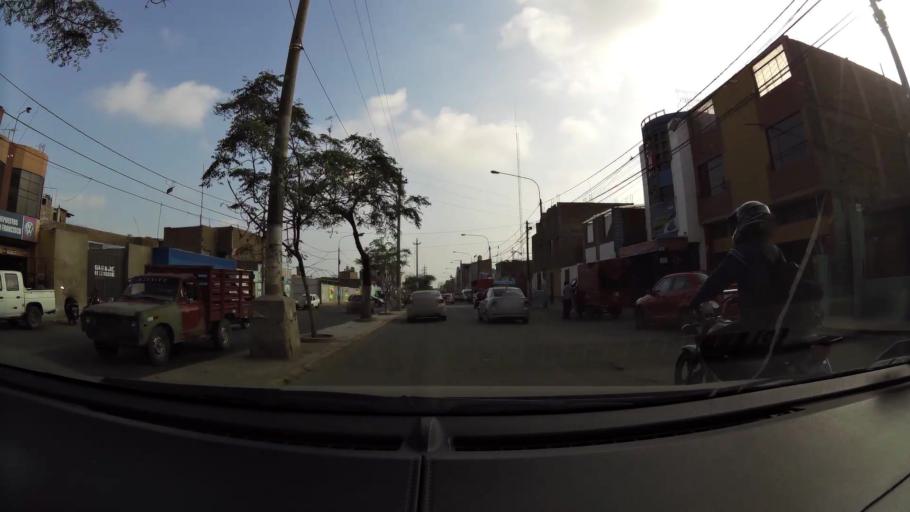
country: PE
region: La Libertad
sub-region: Provincia de Trujillo
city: Trujillo
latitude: -8.1028
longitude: -79.0176
